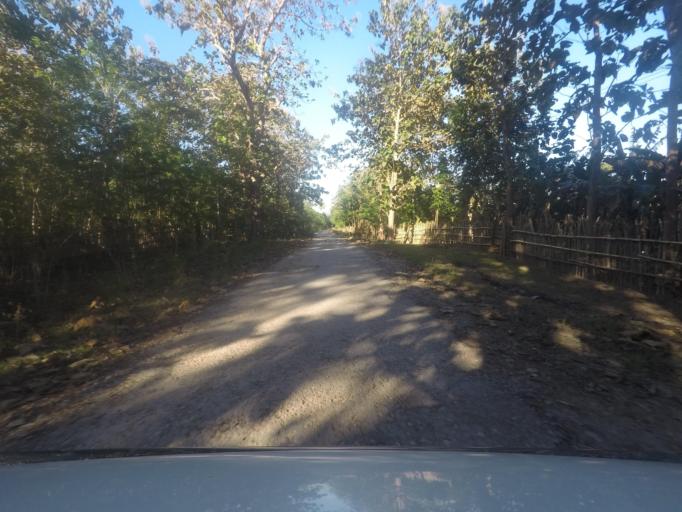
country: TL
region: Lautem
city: Lospalos
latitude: -8.4098
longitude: 127.1629
